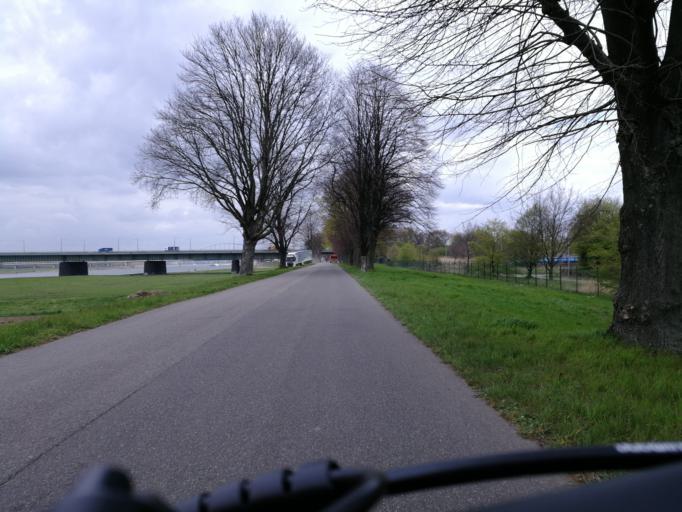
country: DE
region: North Rhine-Westphalia
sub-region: Regierungsbezirk Dusseldorf
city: Dusseldorf
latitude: 51.1953
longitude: 6.7366
